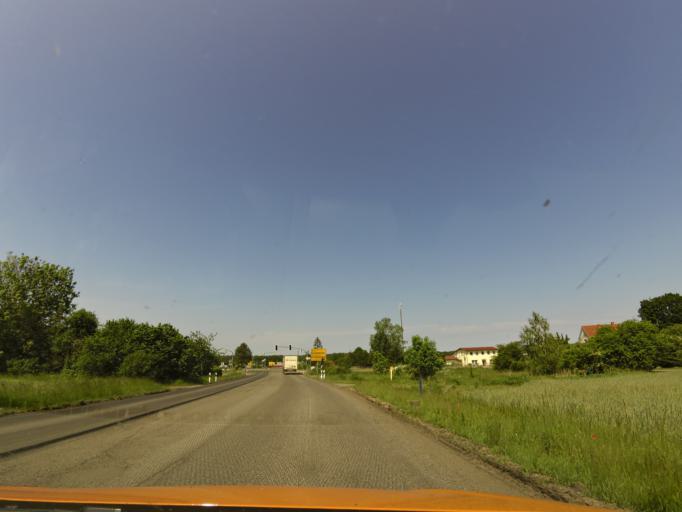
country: DE
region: Mecklenburg-Vorpommern
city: Selmsdorf
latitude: 53.8826
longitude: 10.8651
